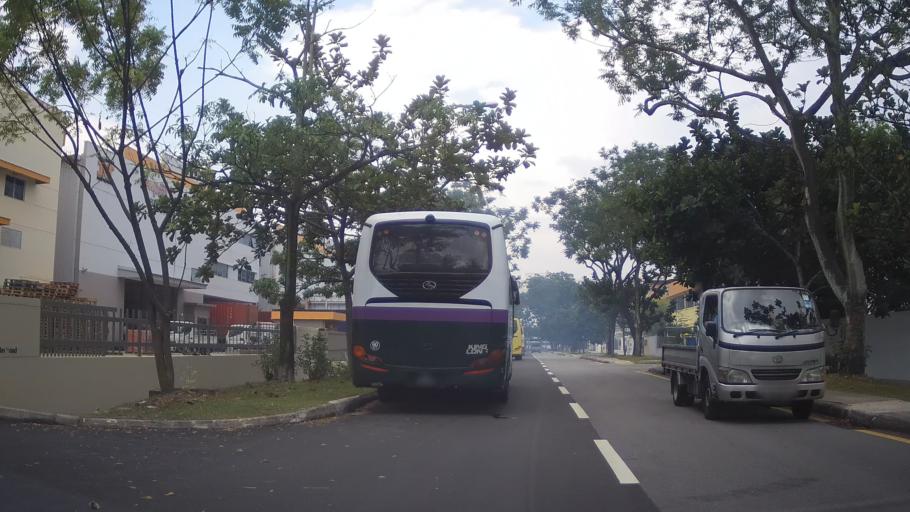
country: MY
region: Johor
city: Johor Bahru
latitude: 1.3307
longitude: 103.7021
